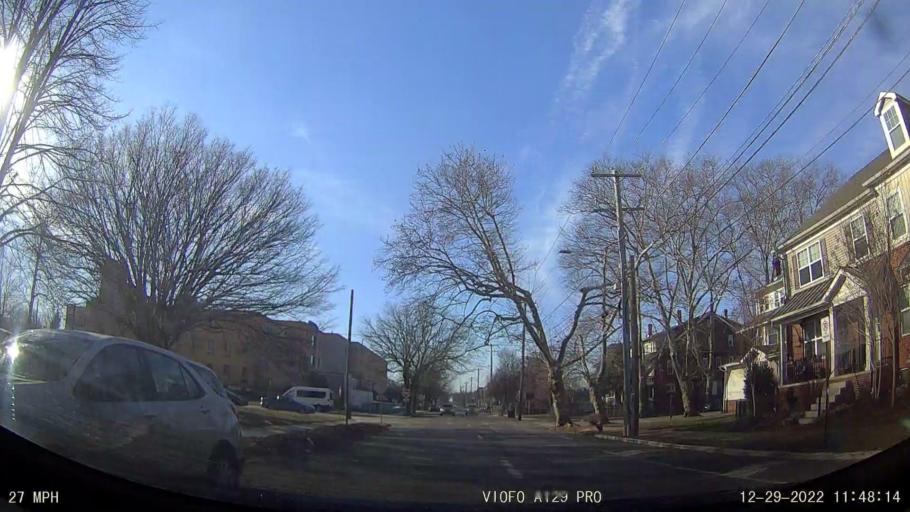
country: US
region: Pennsylvania
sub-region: Montgomery County
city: Norristown
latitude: 40.1245
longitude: -75.3317
